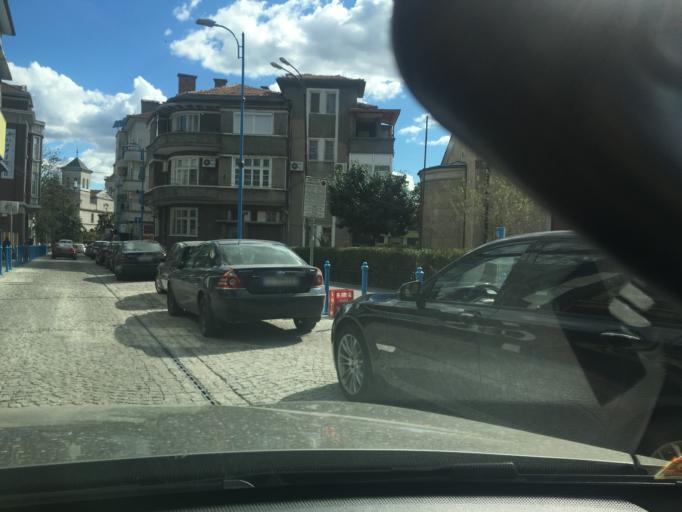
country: BG
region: Burgas
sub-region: Obshtina Burgas
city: Burgas
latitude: 42.4935
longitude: 27.4741
